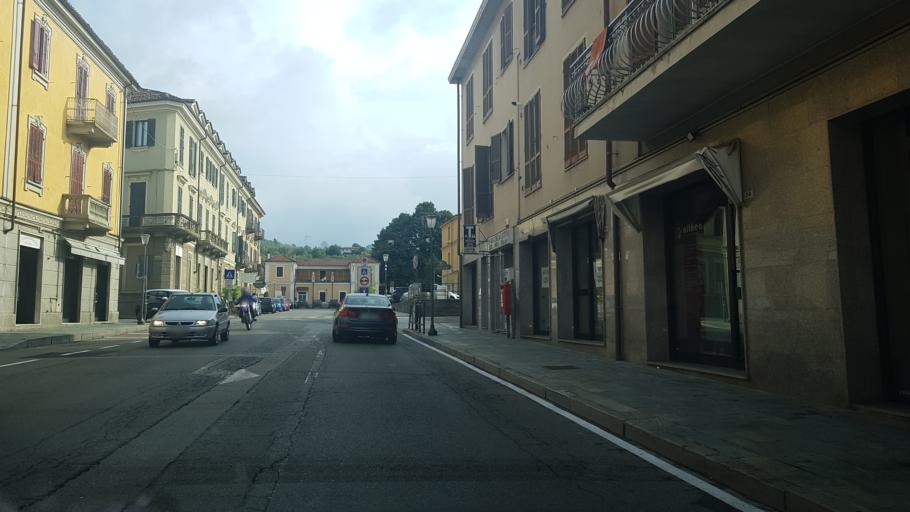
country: IT
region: Piedmont
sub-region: Provincia di Asti
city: Canelli
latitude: 44.7160
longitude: 8.2881
